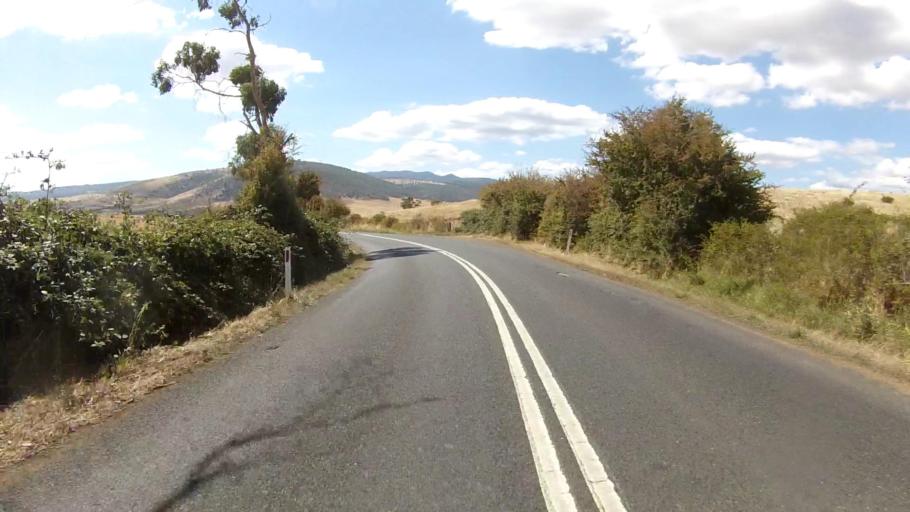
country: AU
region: Tasmania
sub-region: Derwent Valley
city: New Norfolk
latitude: -42.7372
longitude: 146.9353
